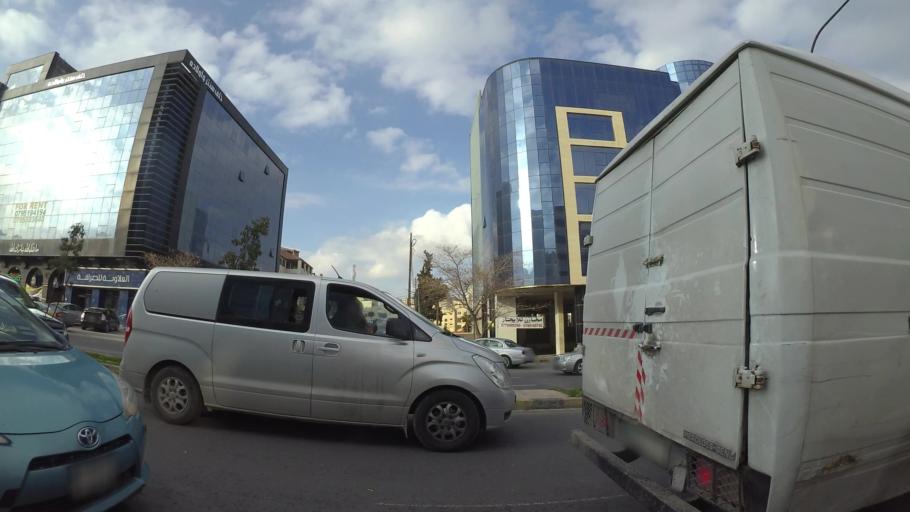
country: JO
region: Amman
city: Al Jubayhah
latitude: 31.9841
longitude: 35.8872
